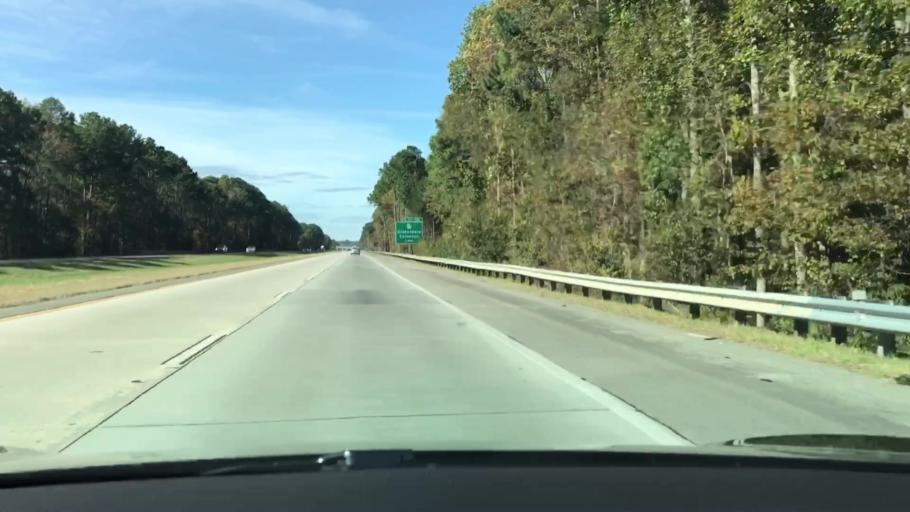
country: US
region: Georgia
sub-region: Greene County
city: Greensboro
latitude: 33.5472
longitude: -83.1813
